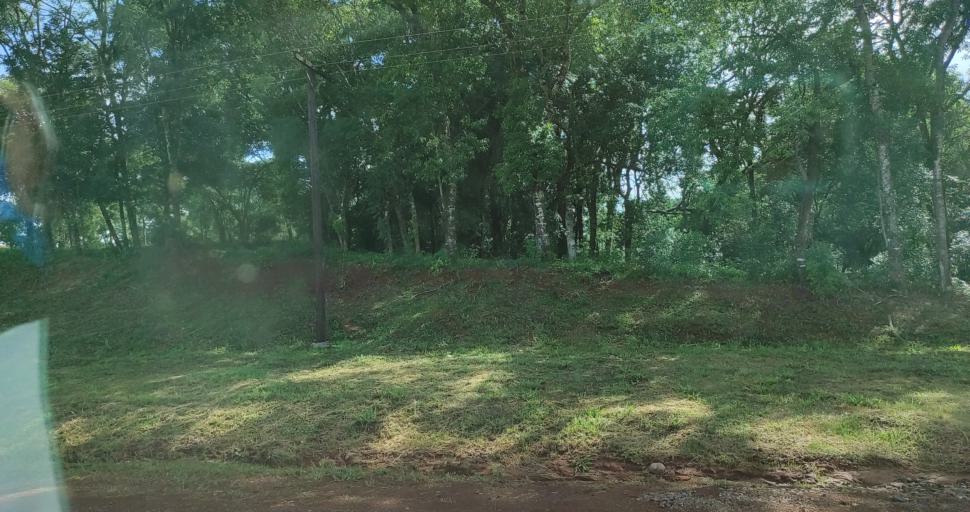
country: AR
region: Misiones
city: Dos de Mayo
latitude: -27.0068
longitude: -54.4893
